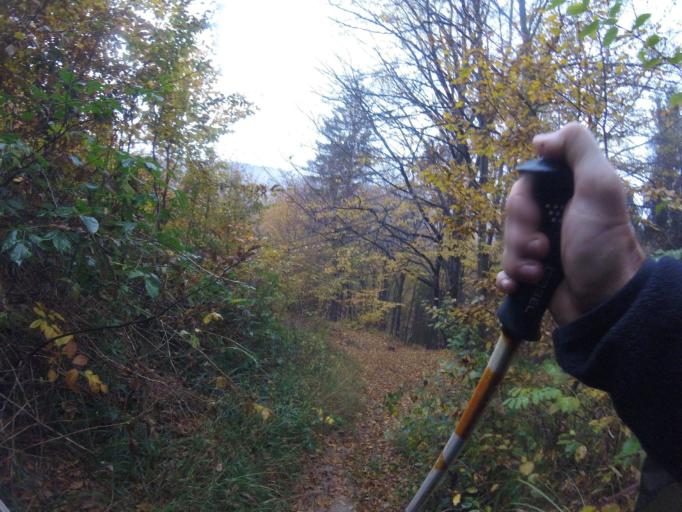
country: HU
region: Borsod-Abauj-Zemplen
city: Gonc
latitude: 48.4570
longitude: 21.3209
